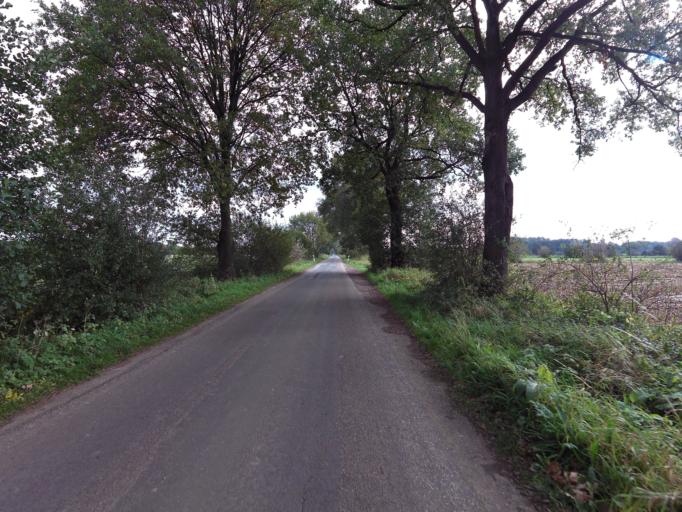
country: DE
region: North Rhine-Westphalia
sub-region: Regierungsbezirk Munster
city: Isselburg
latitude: 51.8222
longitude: 6.4822
